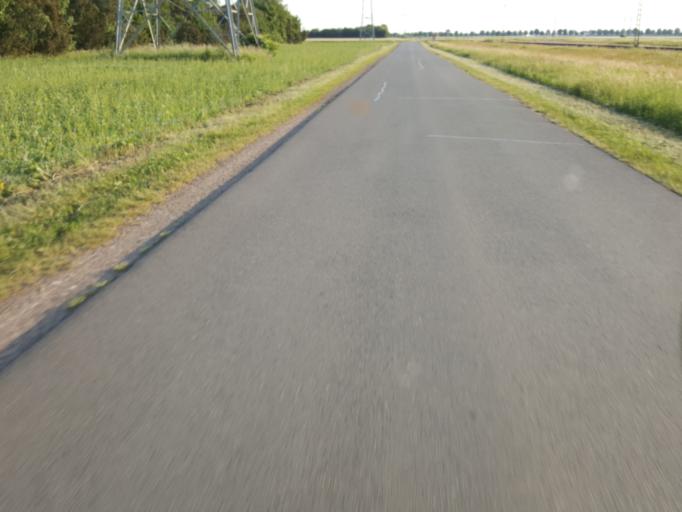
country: DE
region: Lower Saxony
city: Landesbergen
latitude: 52.5386
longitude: 9.1272
